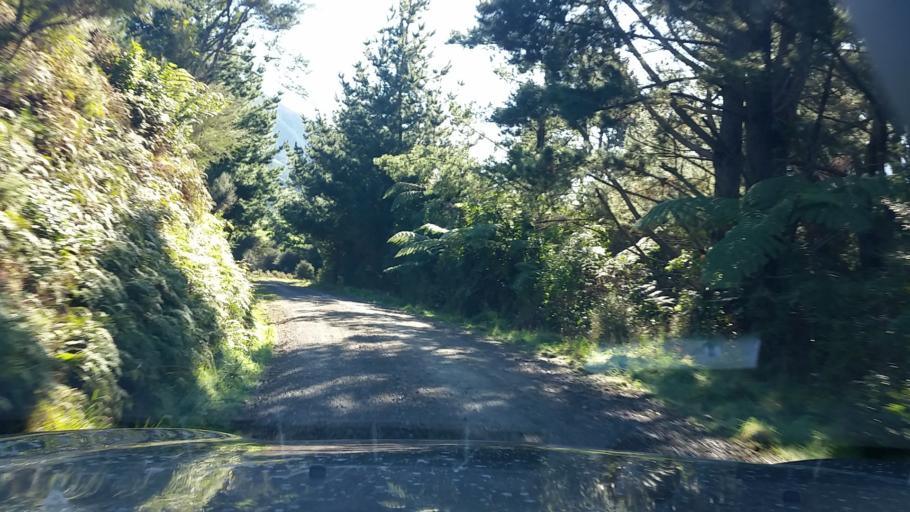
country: NZ
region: Marlborough
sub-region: Marlborough District
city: Picton
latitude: -41.1323
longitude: 174.0398
